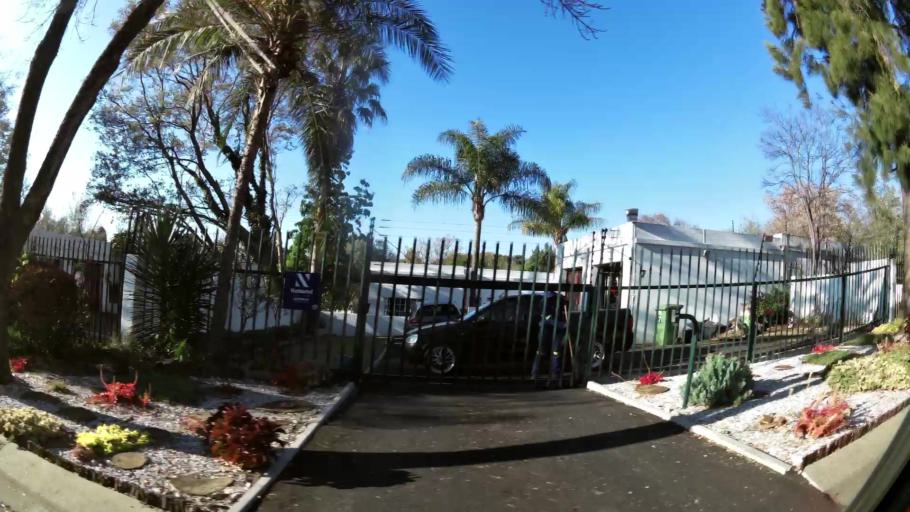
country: ZA
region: Gauteng
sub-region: City of Johannesburg Metropolitan Municipality
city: Midrand
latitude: -26.0305
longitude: 28.0520
